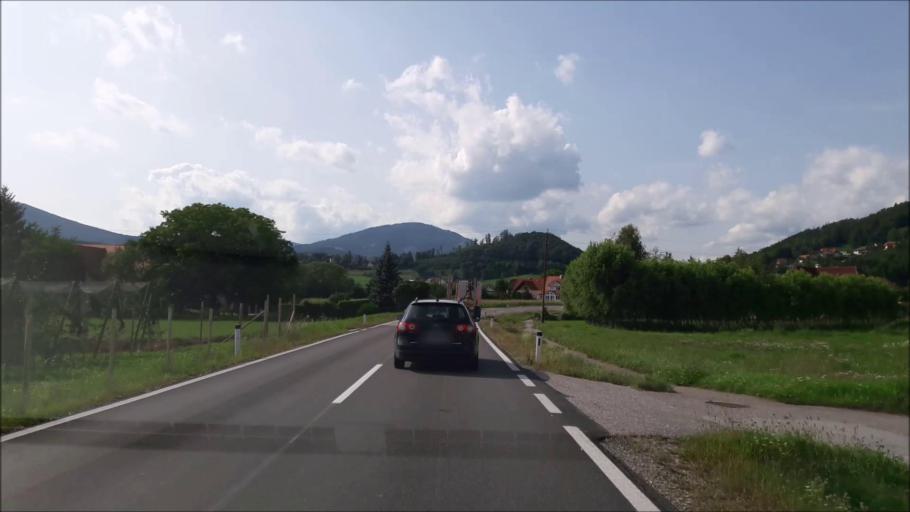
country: AT
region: Styria
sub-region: Politischer Bezirk Weiz
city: Floing
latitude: 47.2448
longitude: 15.7336
